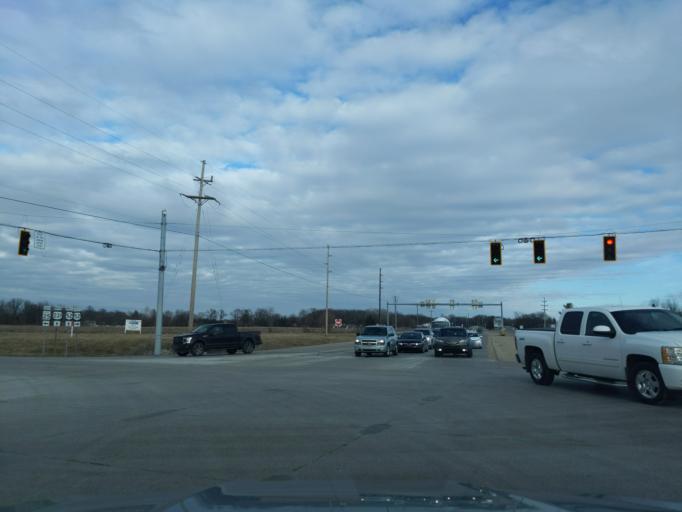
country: US
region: Indiana
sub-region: Tippecanoe County
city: Shadeland
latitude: 40.3869
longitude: -86.9188
